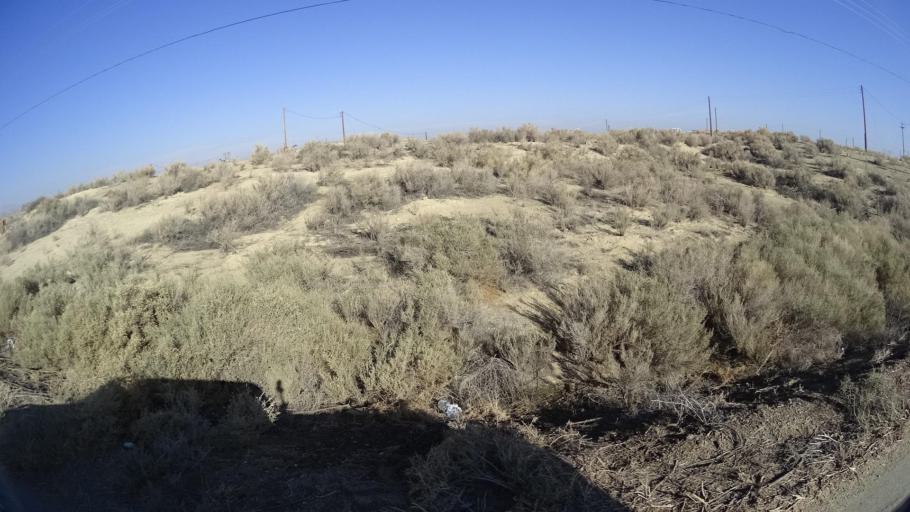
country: US
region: California
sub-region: Kern County
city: Taft Heights
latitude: 35.2194
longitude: -119.6056
